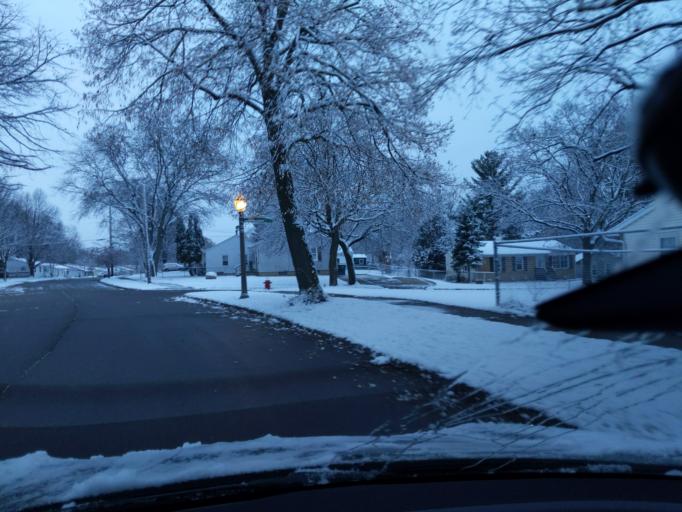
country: US
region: Michigan
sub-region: Ingham County
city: Lansing
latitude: 42.6864
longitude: -84.5589
